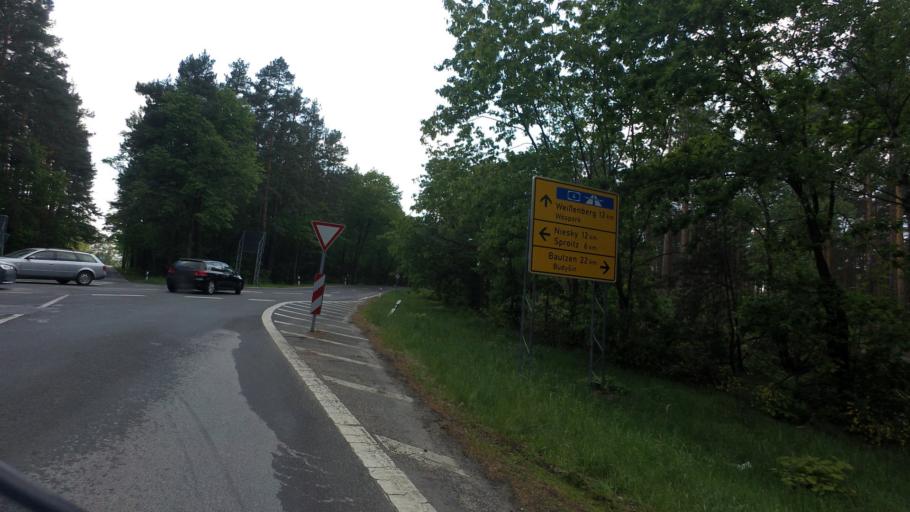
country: DE
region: Saxony
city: Mucka
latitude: 51.2835
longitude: 14.6564
